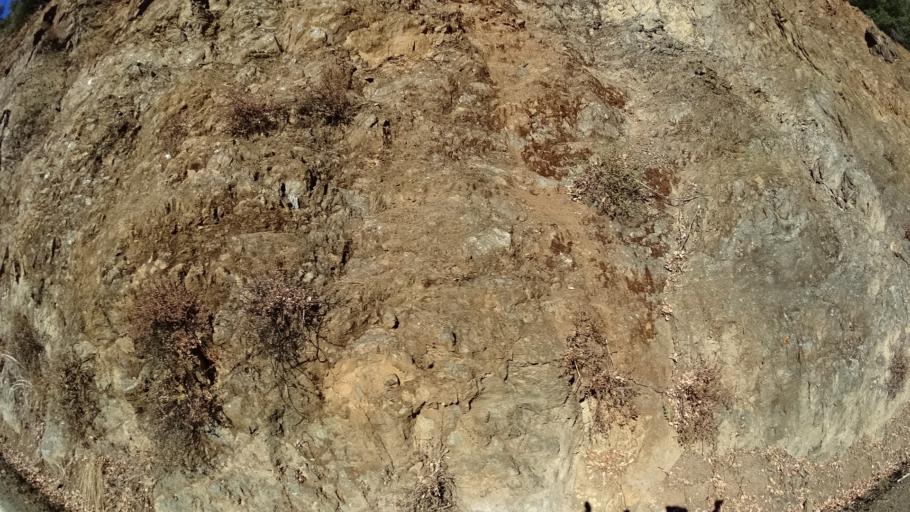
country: US
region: California
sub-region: Trinity County
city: Weaverville
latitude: 41.1714
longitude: -123.0954
